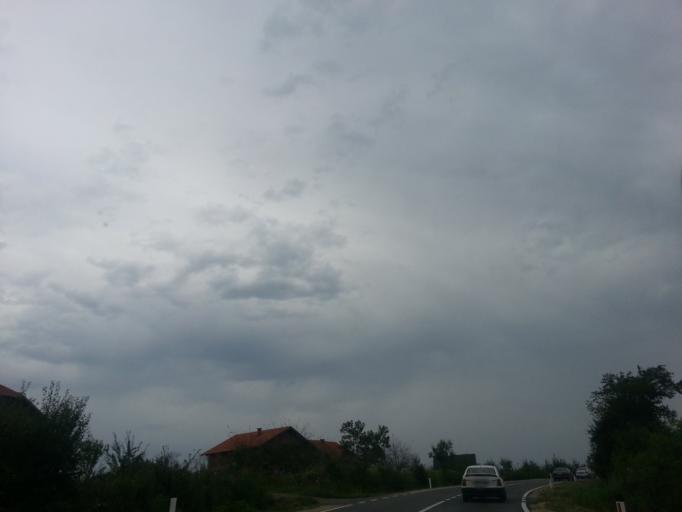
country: HR
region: Vukovarsko-Srijemska
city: Gunja
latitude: 44.8471
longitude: 18.9458
